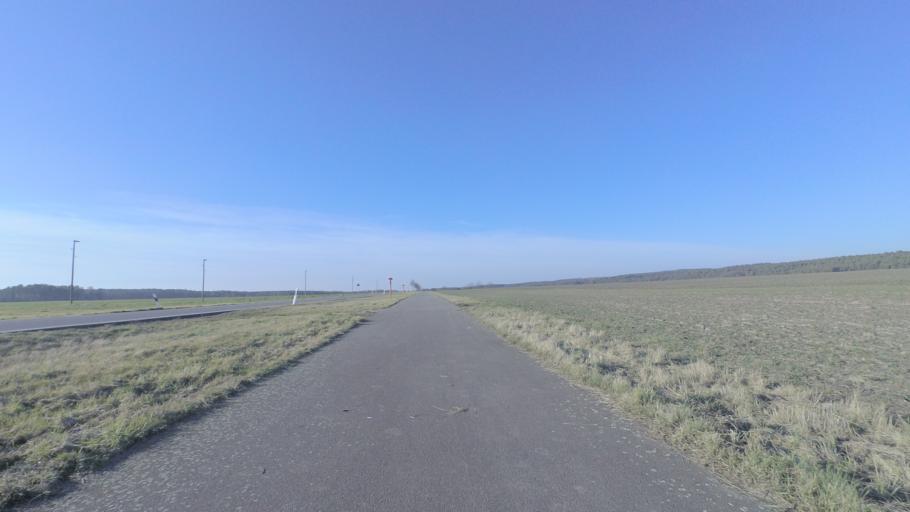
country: DE
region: Brandenburg
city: Ihlow
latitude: 51.9920
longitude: 13.3559
